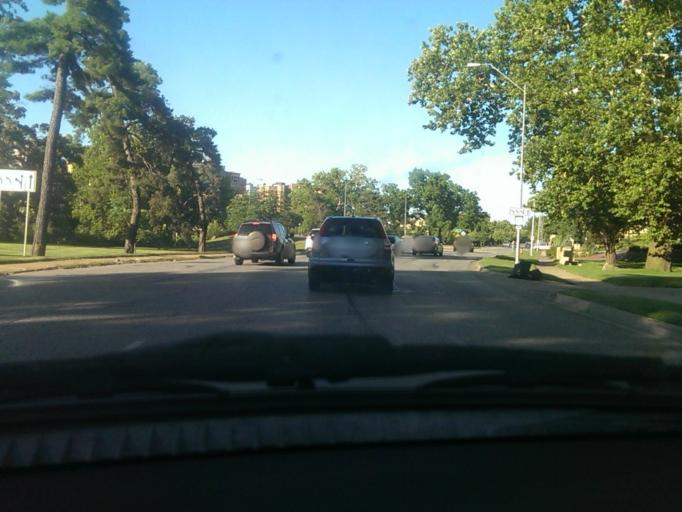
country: US
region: Kansas
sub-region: Johnson County
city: Westwood
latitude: 39.0380
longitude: -94.5988
